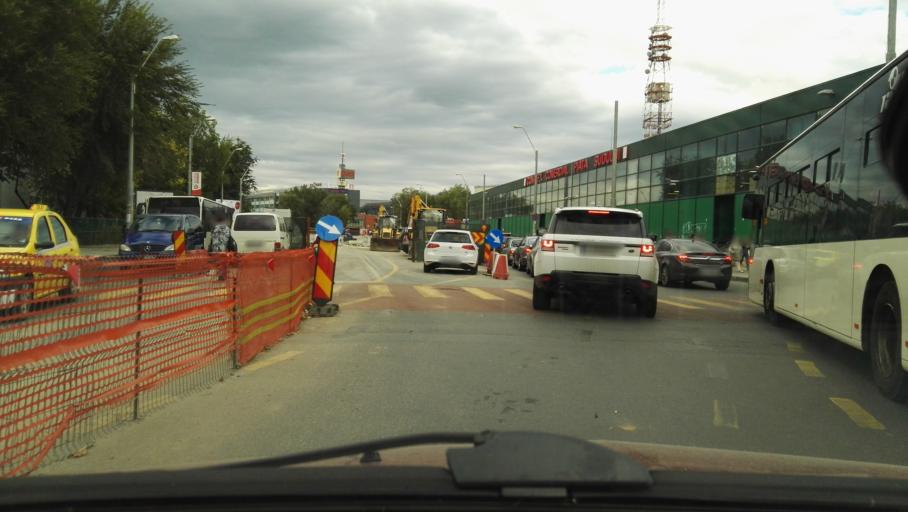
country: RO
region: Bucuresti
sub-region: Municipiul Bucuresti
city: Bucharest
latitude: 44.3915
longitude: 26.1200
